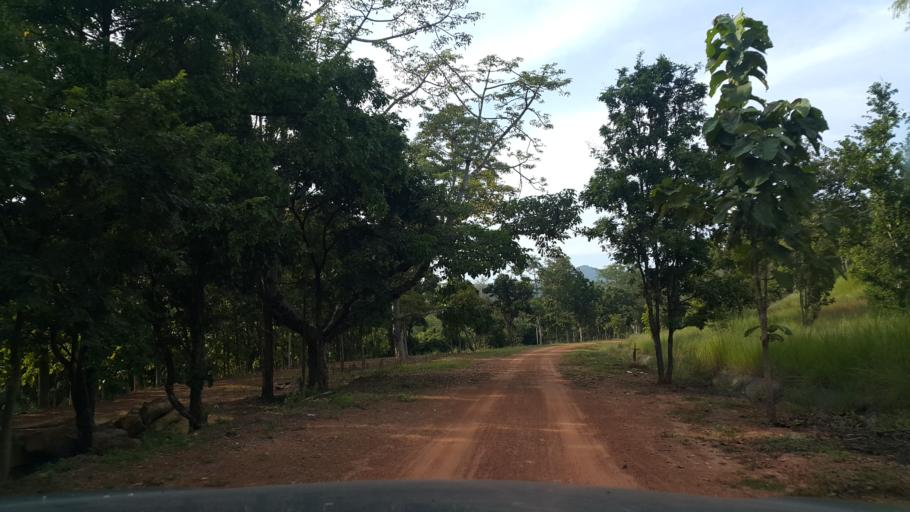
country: TH
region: Chiang Mai
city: San Sai
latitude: 18.9147
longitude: 99.1014
